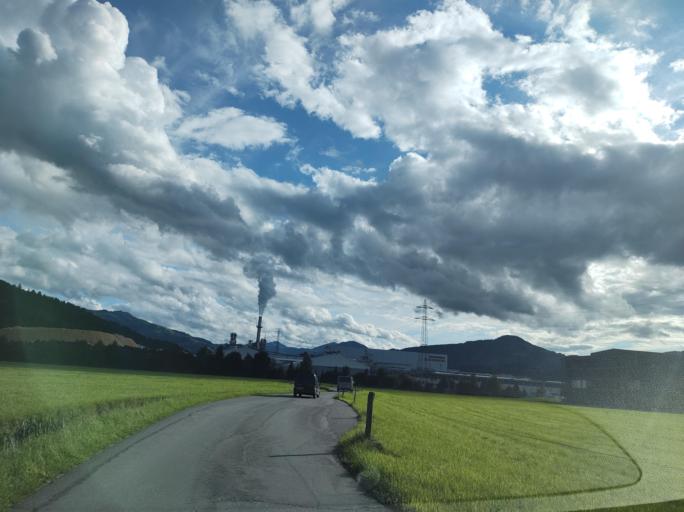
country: AT
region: Tyrol
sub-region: Politischer Bezirk Kitzbuhel
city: Sankt Johann in Tirol
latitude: 47.5096
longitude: 12.4058
